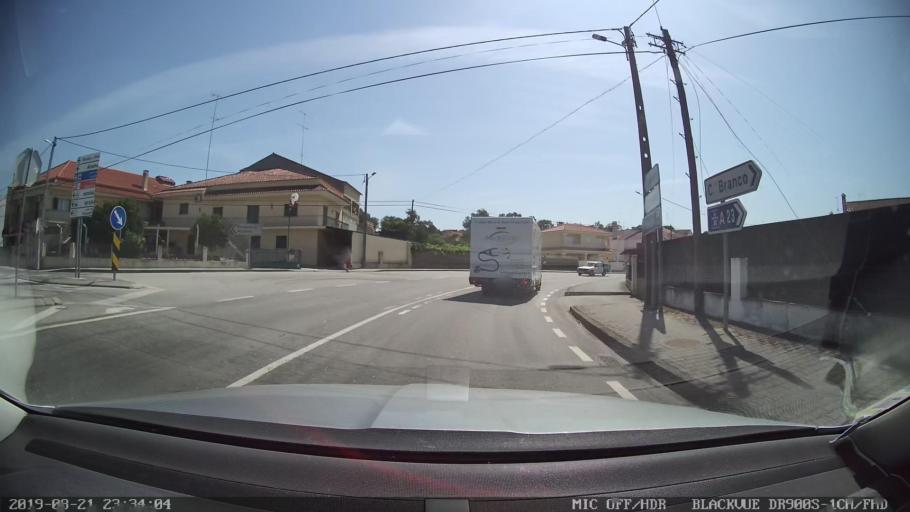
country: PT
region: Guarda
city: Alcains
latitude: 39.8834
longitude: -7.3976
